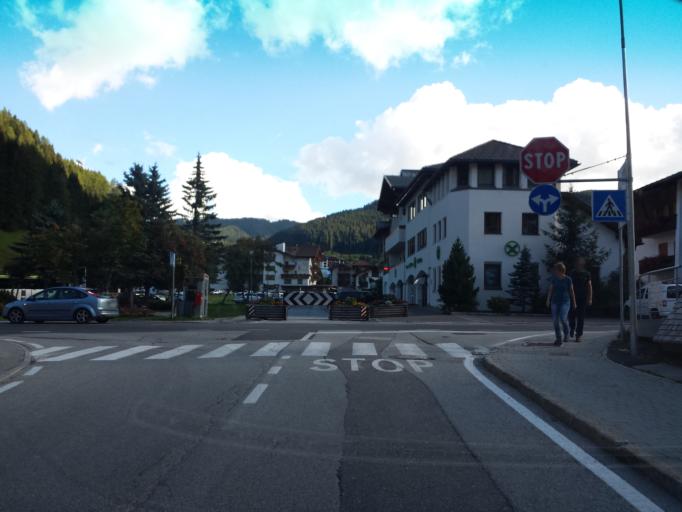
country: IT
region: Trentino-Alto Adige
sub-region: Bolzano
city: Corvara in Badia
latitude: 46.5524
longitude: 11.8736
